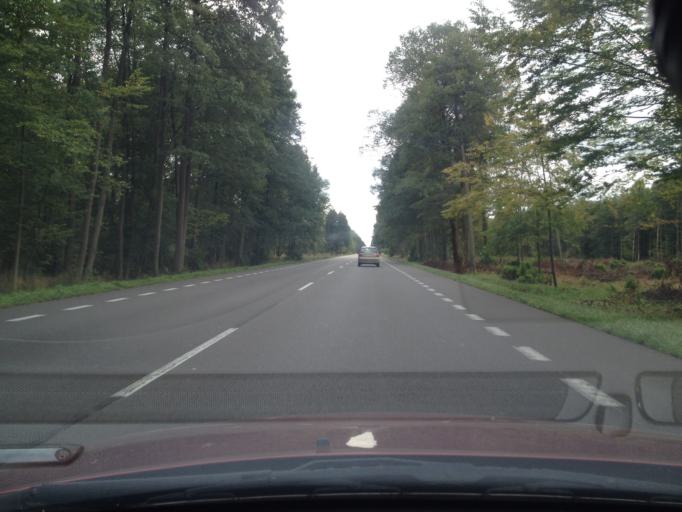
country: PL
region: West Pomeranian Voivodeship
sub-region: Powiat goleniowski
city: Przybiernow
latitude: 53.6652
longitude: 14.8148
